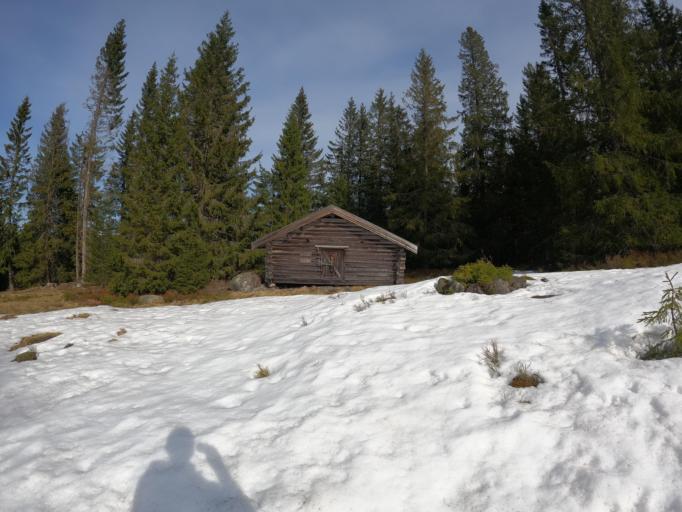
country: NO
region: Akershus
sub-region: Nannestad
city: Teigebyen
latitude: 60.2491
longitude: 10.8896
